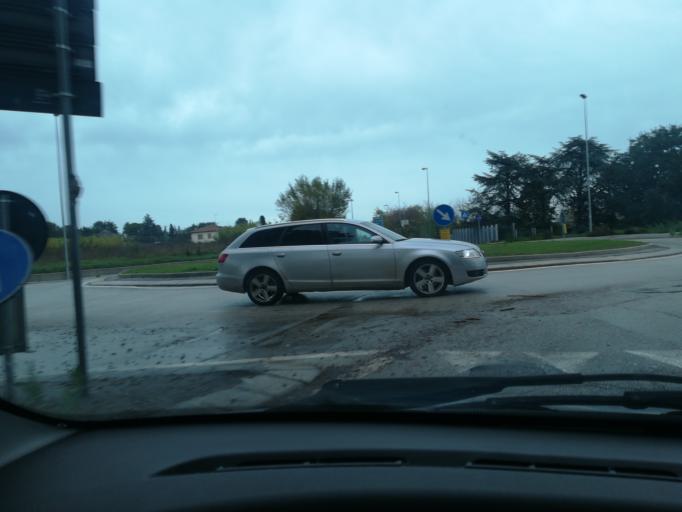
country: IT
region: The Marches
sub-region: Provincia di Macerata
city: Santa Maria Apparente
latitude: 43.2988
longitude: 13.7003
